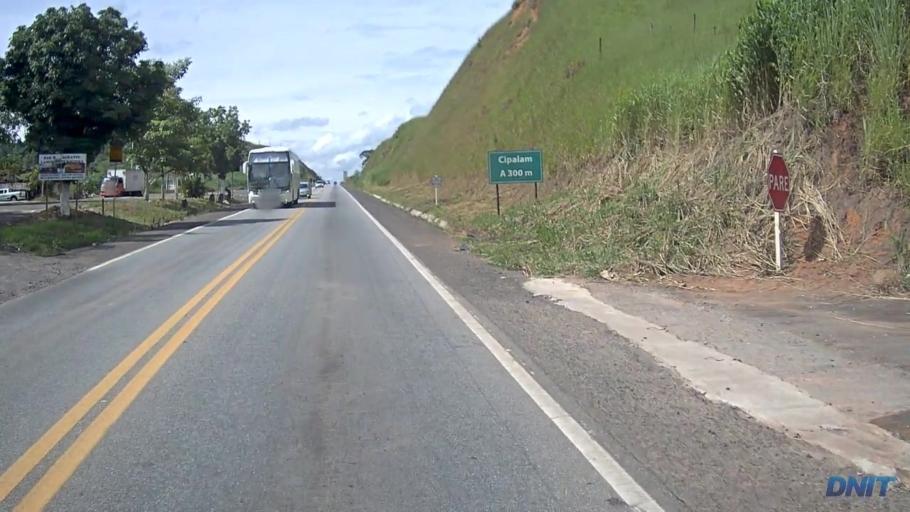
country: BR
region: Minas Gerais
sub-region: Ipatinga
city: Ipatinga
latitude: -19.4206
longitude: -42.4943
